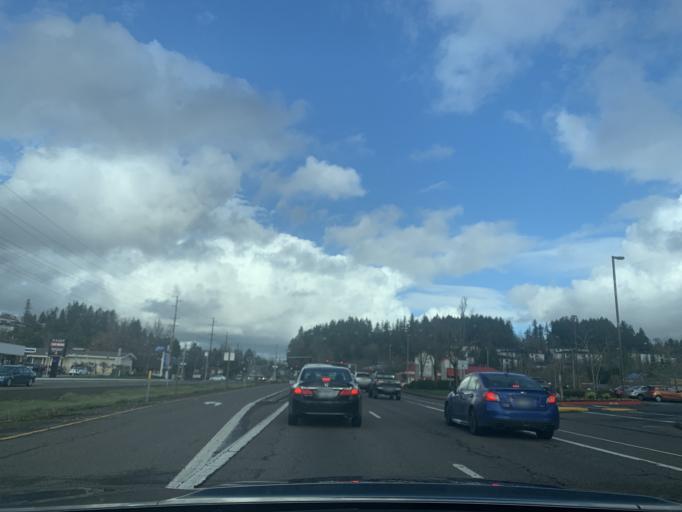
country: US
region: Oregon
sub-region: Washington County
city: King City
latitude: 45.4067
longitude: -122.7955
